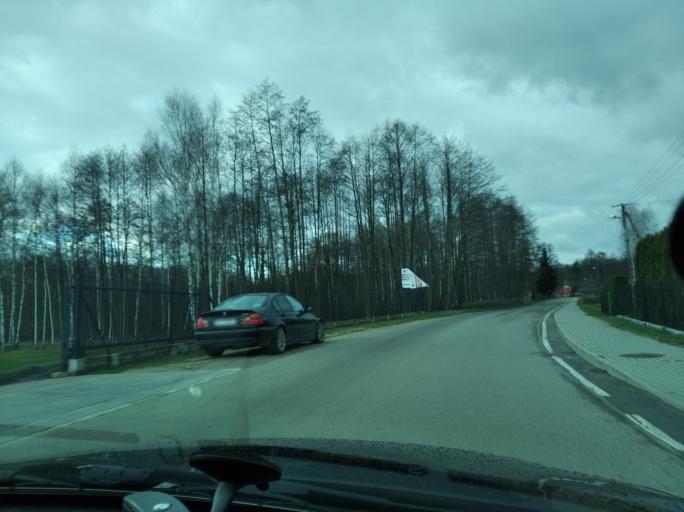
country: PL
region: Subcarpathian Voivodeship
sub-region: Powiat lancucki
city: Zolynia
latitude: 50.1456
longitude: 22.2766
